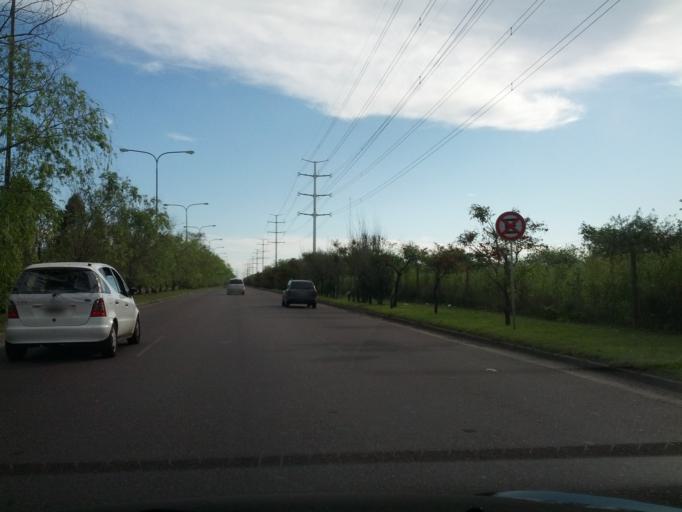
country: AR
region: Buenos Aires F.D.
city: Villa Lugano
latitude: -34.6937
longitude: -58.4519
